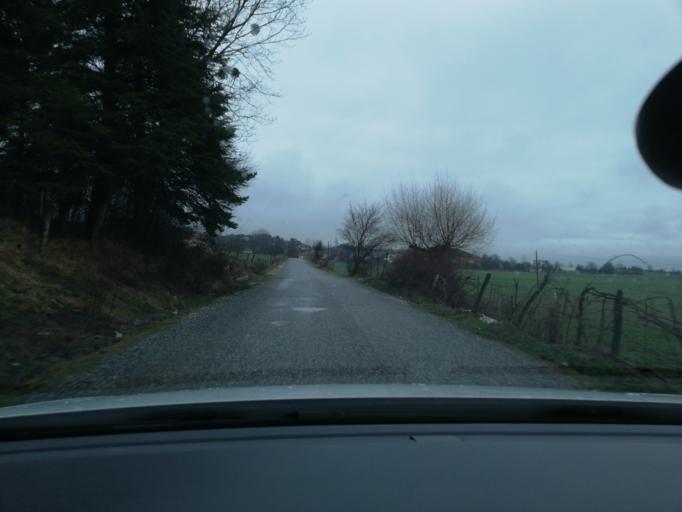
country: TR
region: Bolu
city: Bolu
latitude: 40.7722
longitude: 31.6526
